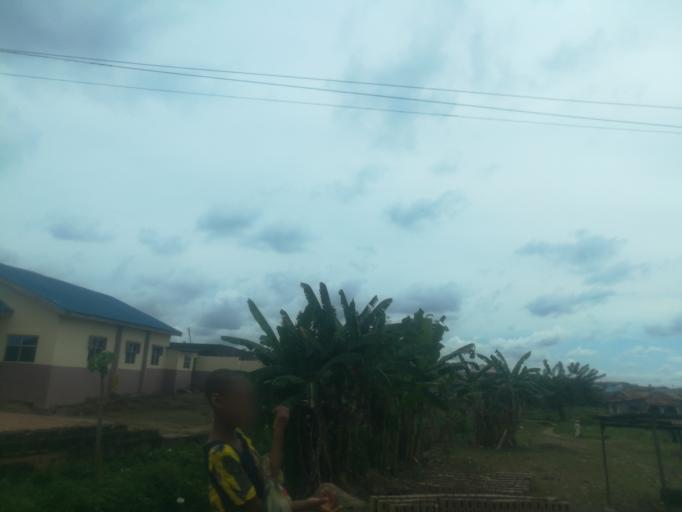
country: NG
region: Oyo
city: Ibadan
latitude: 7.3744
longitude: 3.9697
